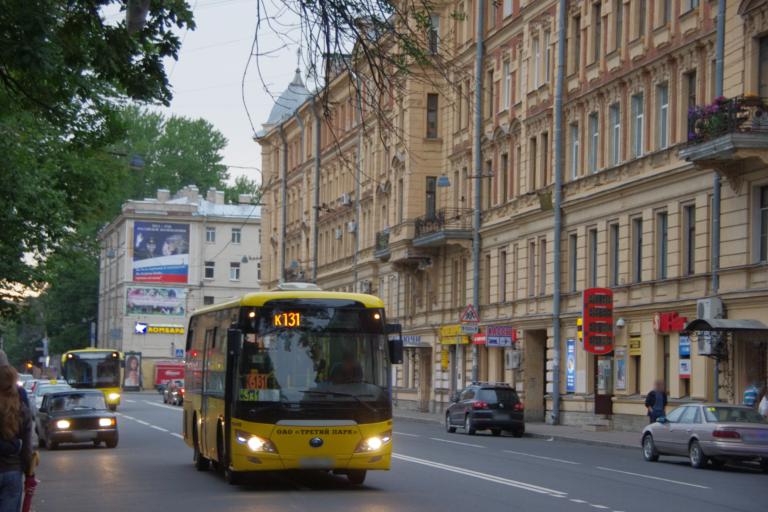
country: RU
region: St.-Petersburg
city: Petrogradka
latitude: 59.9606
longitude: 30.2934
